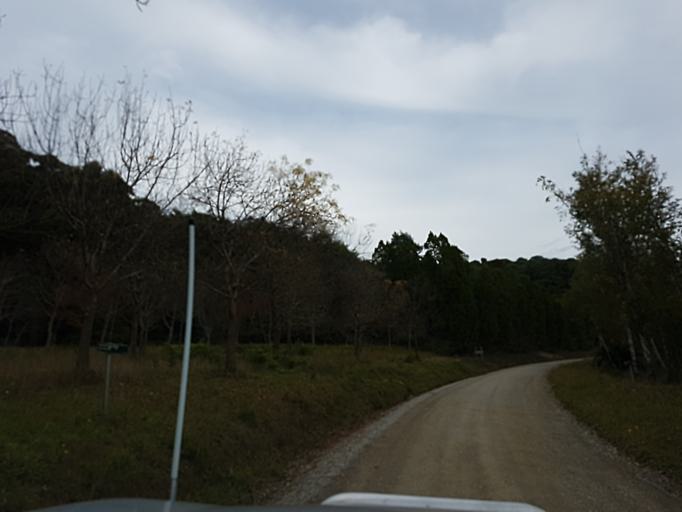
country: AU
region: Victoria
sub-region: Yarra Ranges
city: Olinda
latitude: -37.8561
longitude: 145.3889
